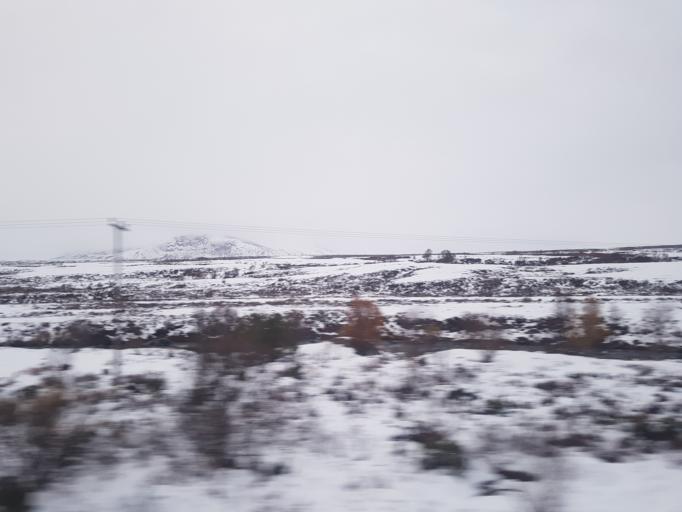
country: NO
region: Sor-Trondelag
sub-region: Oppdal
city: Oppdal
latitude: 62.2725
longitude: 9.5801
